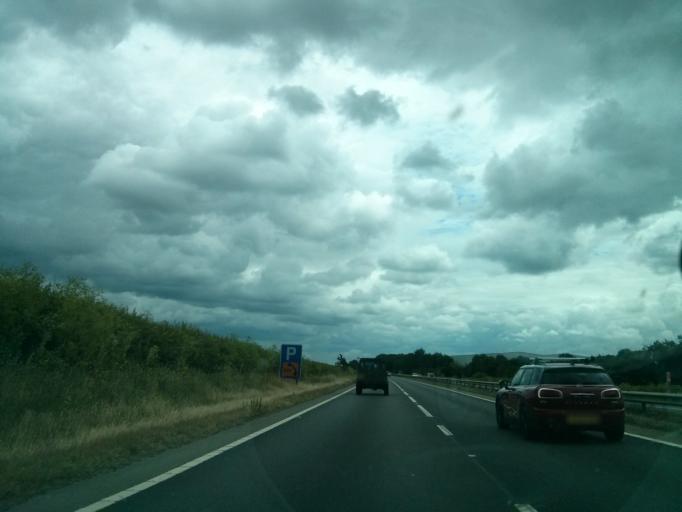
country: GB
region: England
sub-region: Suffolk
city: Bury St Edmunds
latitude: 52.2594
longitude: 0.6405
